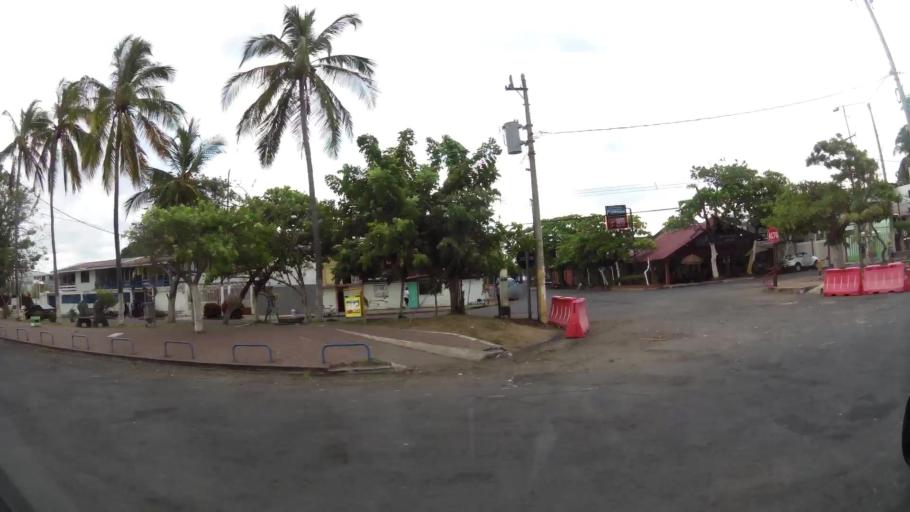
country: CR
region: Puntarenas
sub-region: Canton Central de Puntarenas
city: Puntarenas
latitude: 9.9746
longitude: -84.8435
